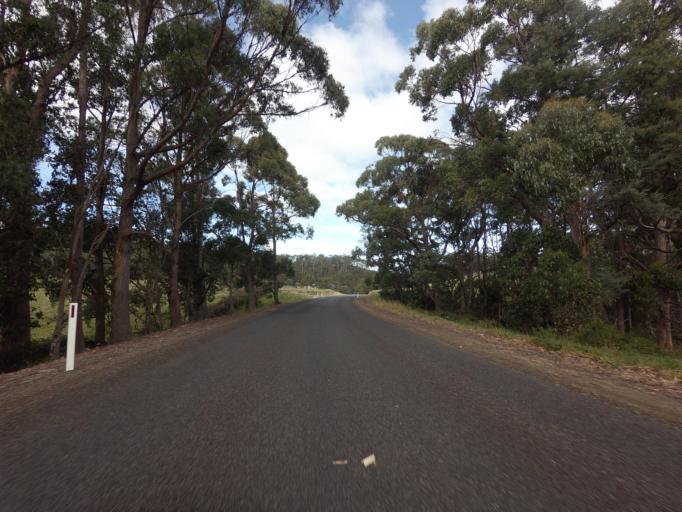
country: AU
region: Tasmania
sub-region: Clarence
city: Sandford
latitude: -43.0748
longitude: 147.7497
